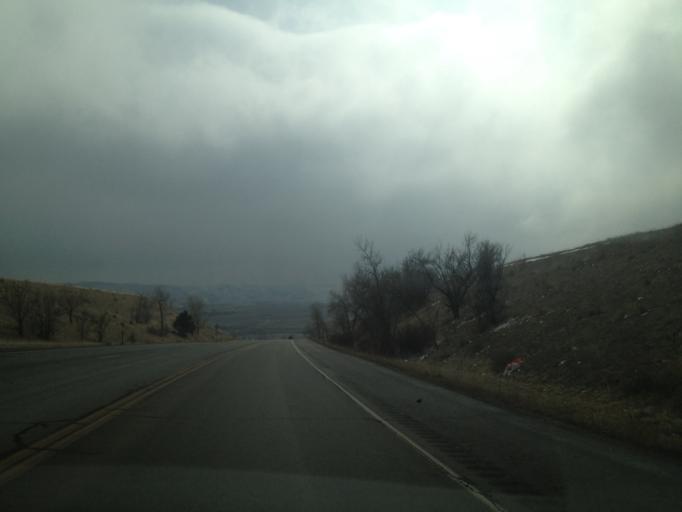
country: US
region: Colorado
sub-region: Jefferson County
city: Golden
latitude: 39.8331
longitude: -105.2286
